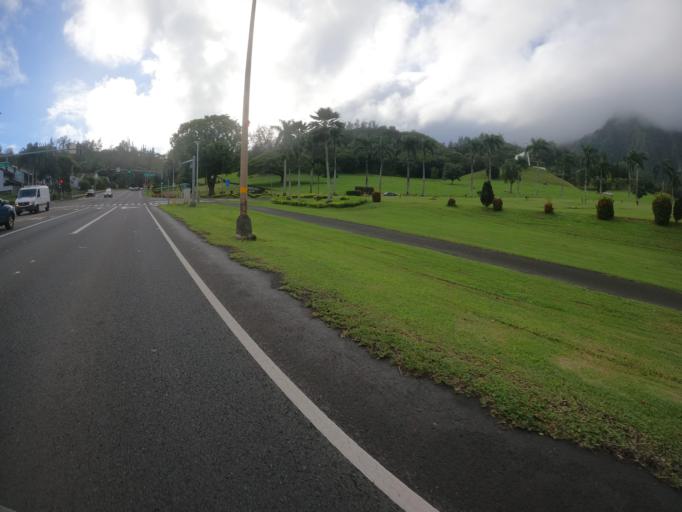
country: US
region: Hawaii
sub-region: Honolulu County
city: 'Ahuimanu
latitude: 21.4352
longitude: -157.8267
